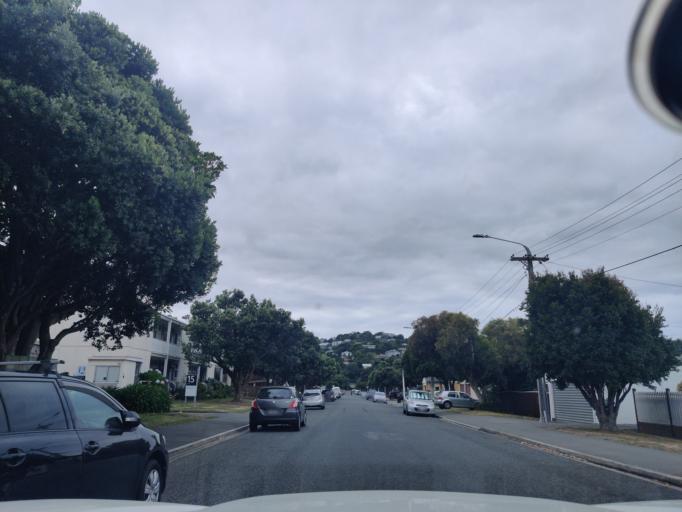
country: NZ
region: Wellington
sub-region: Wellington City
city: Wellington
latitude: -41.3117
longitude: 174.8174
